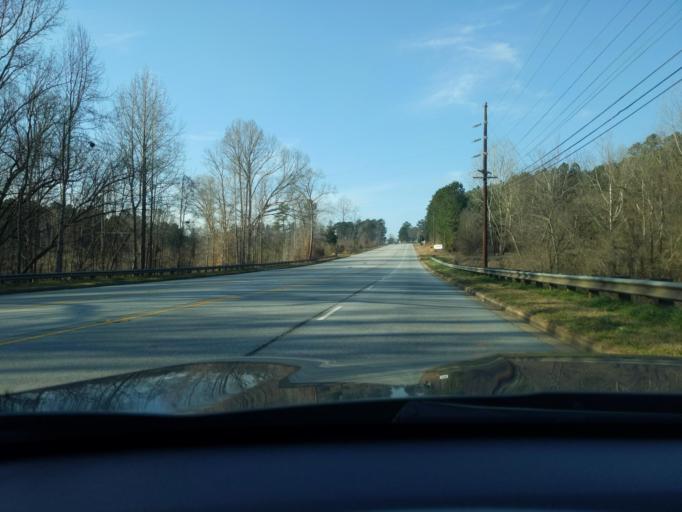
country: US
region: South Carolina
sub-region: Abbeville County
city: Abbeville
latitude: 34.1802
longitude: -82.3630
